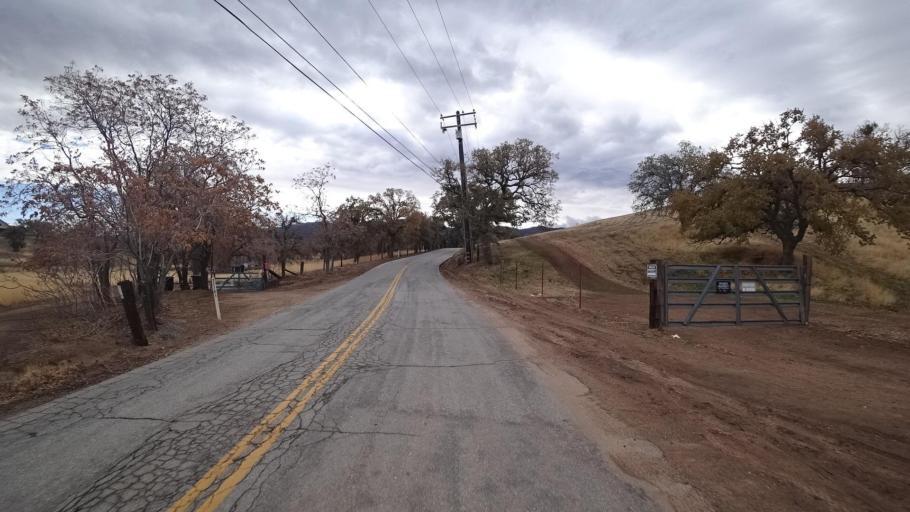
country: US
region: California
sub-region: Kern County
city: Golden Hills
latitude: 35.1285
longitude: -118.5081
